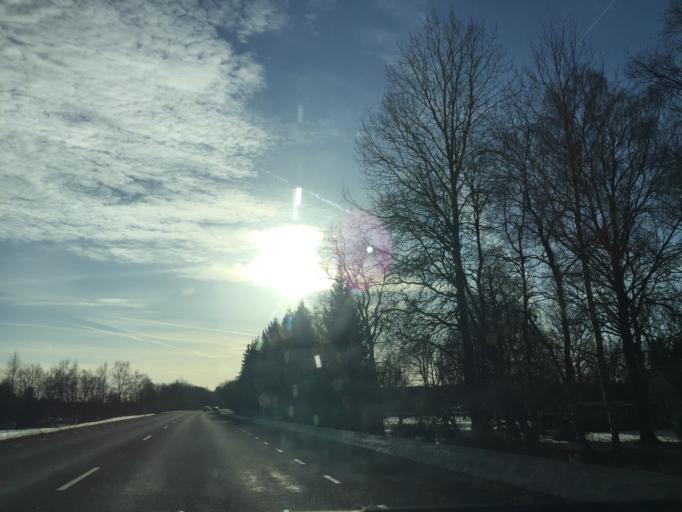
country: EE
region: Saare
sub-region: Kuressaare linn
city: Kuressaare
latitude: 58.3632
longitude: 22.7188
